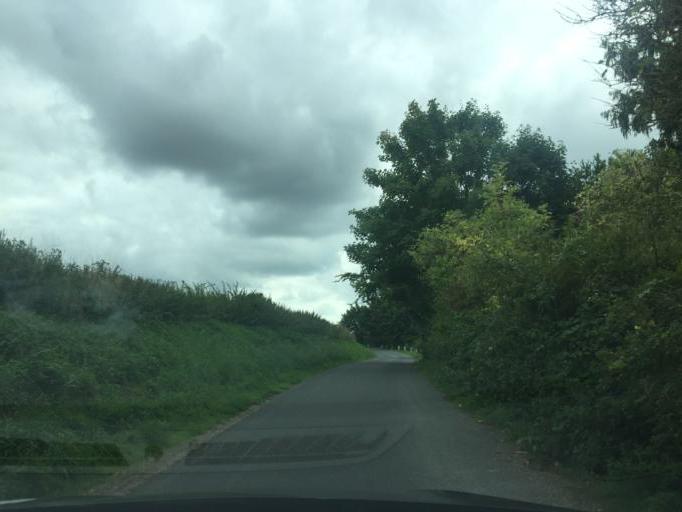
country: DK
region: South Denmark
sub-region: Assens Kommune
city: Tommerup
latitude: 55.3602
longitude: 10.2192
